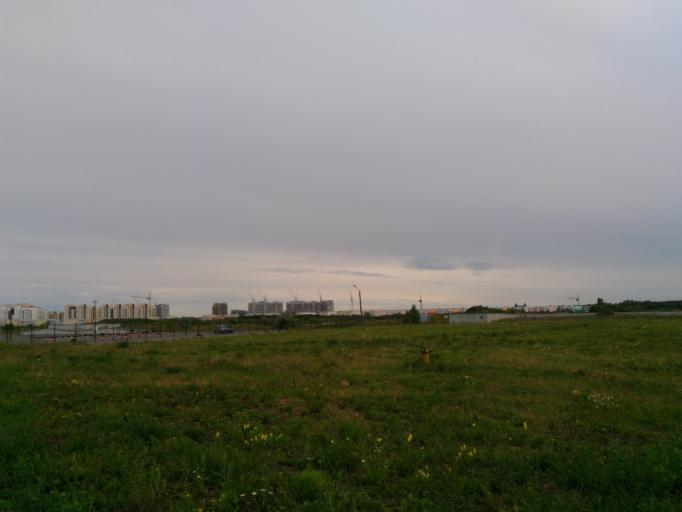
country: RU
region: Ulyanovsk
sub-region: Ulyanovskiy Rayon
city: Ulyanovsk
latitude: 54.2902
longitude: 48.2723
